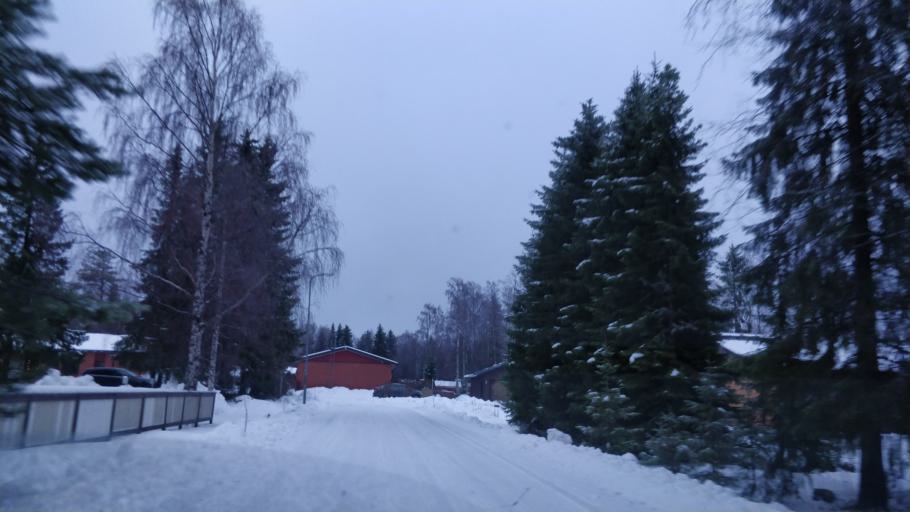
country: FI
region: Lapland
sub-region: Kemi-Tornio
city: Kemi
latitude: 65.7415
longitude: 24.6000
